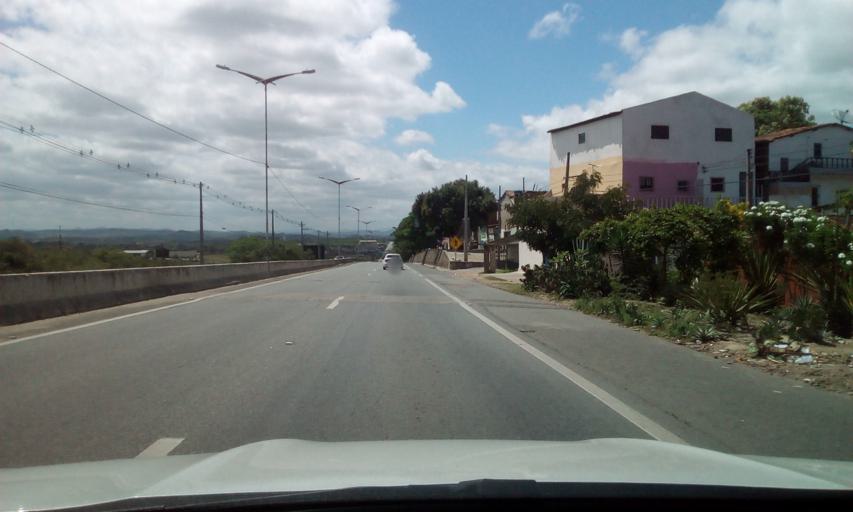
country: BR
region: Paraiba
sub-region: Campina Grande
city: Campina Grande
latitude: -7.2386
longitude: -35.8648
